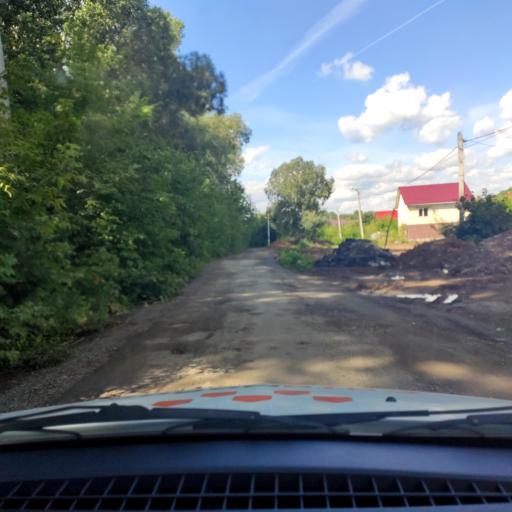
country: RU
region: Bashkortostan
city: Ufa
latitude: 54.7100
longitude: 55.9357
